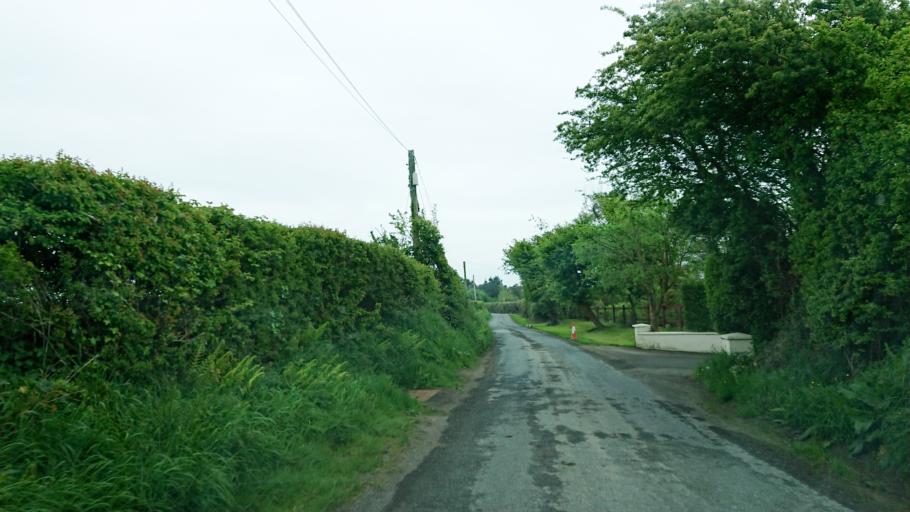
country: IE
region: Munster
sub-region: Waterford
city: Dunmore East
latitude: 52.2250
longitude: -7.0256
